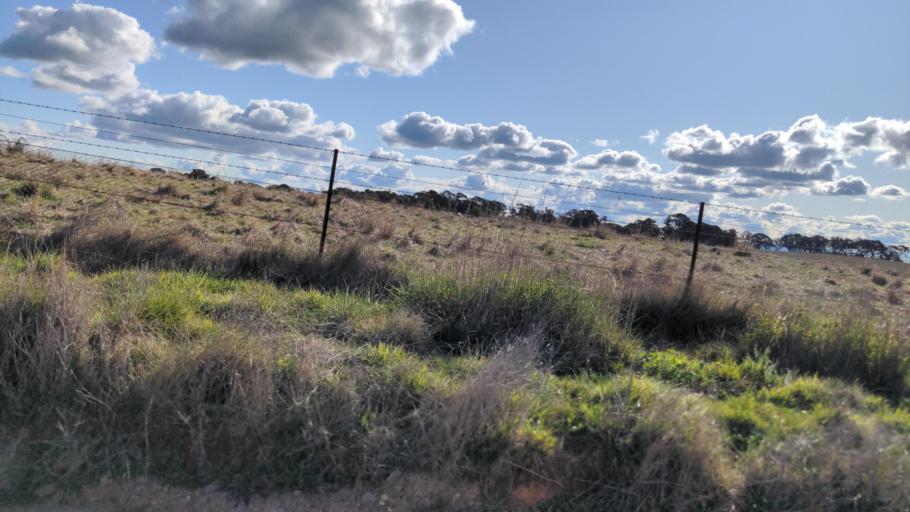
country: AU
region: New South Wales
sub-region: Blayney
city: Blayney
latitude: -33.4243
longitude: 149.3137
